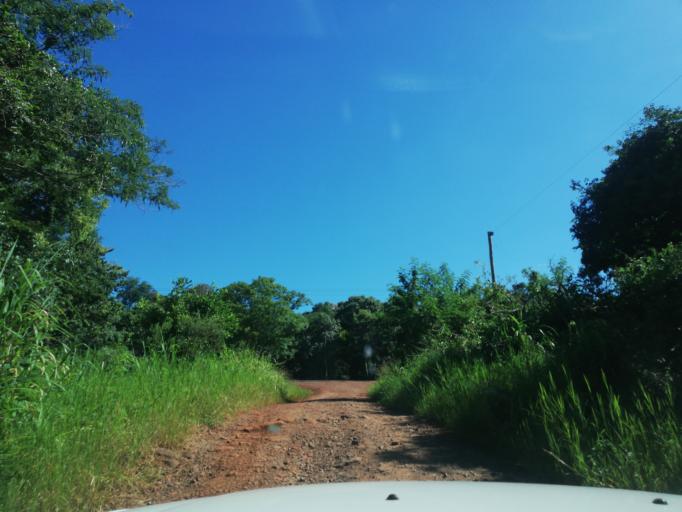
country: AR
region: Misiones
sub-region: Departamento de Leandro N. Alem
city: Leandro N. Alem
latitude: -27.5795
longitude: -55.3738
